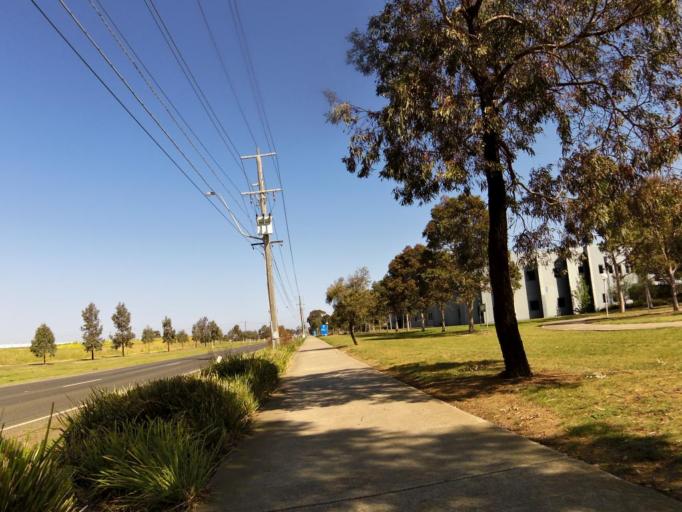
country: AU
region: Victoria
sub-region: Wyndham
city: Hoppers Crossing
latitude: -37.8885
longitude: 144.7005
